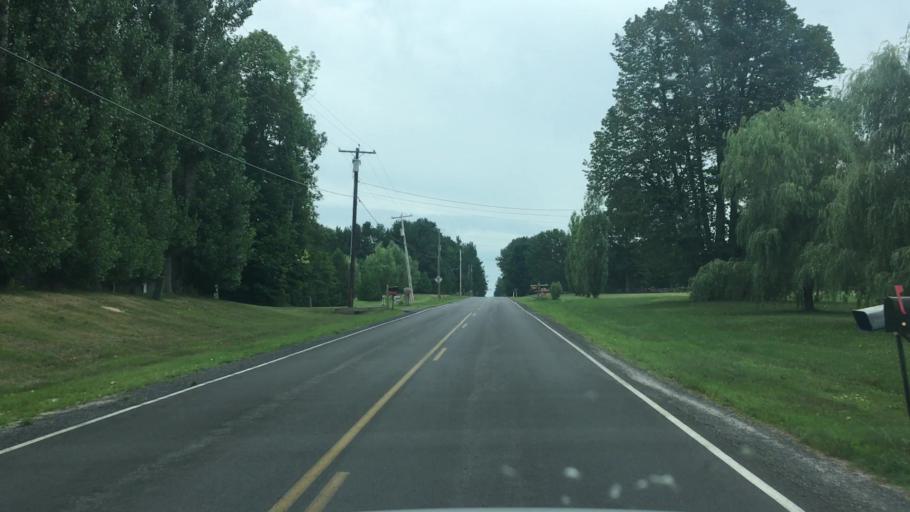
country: US
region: New York
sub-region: Clinton County
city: Peru
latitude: 44.6089
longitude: -73.6299
